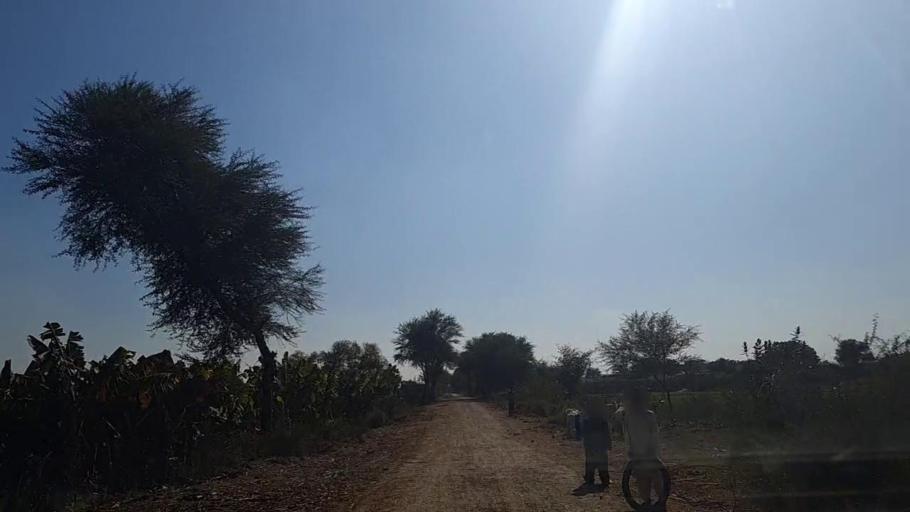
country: PK
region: Sindh
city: Sakrand
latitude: 26.2361
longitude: 68.1998
